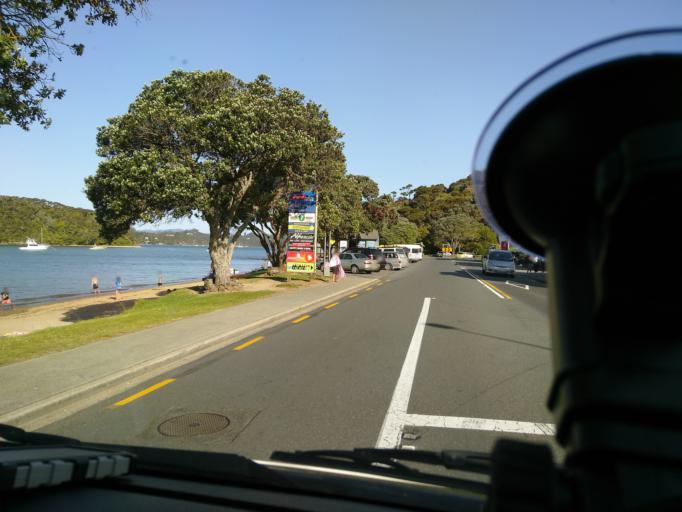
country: NZ
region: Northland
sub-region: Far North District
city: Paihia
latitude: -35.2845
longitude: 174.0956
